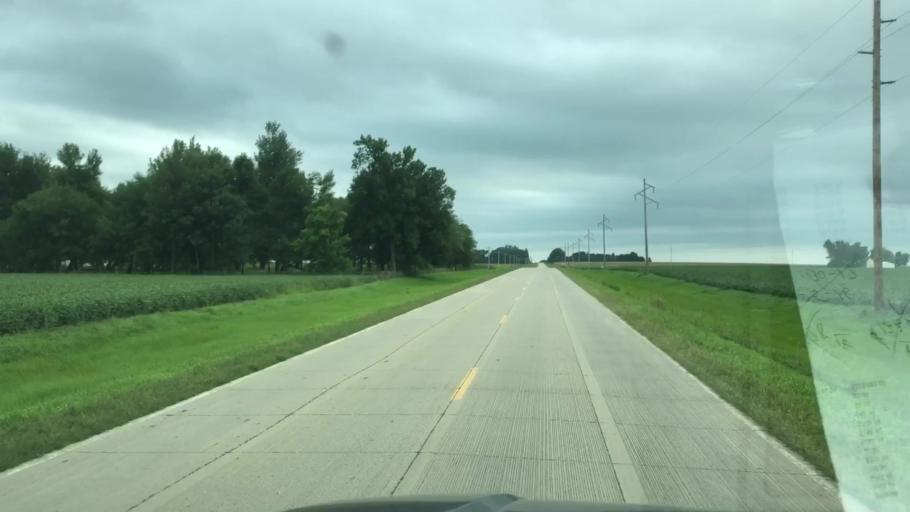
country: US
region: Iowa
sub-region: O'Brien County
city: Sheldon
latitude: 43.1780
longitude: -95.9801
